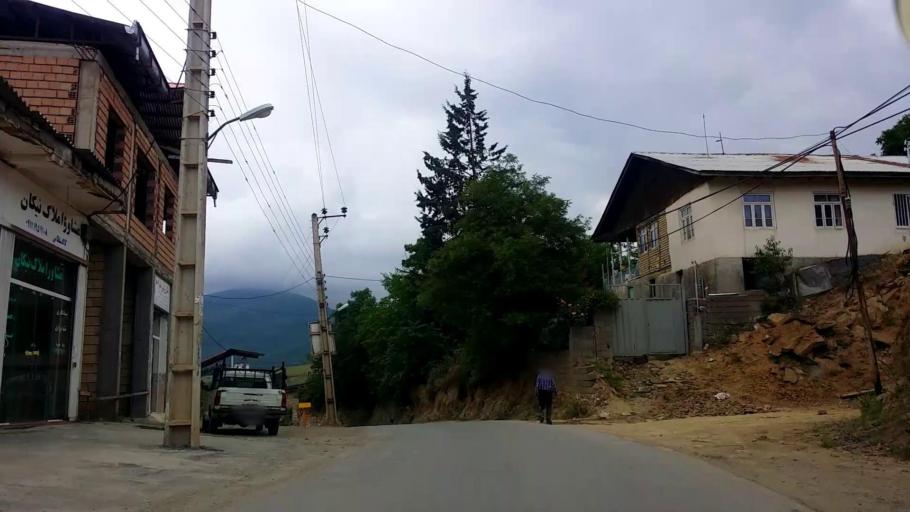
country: IR
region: Mazandaran
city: Chalus
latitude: 36.5148
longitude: 51.2588
